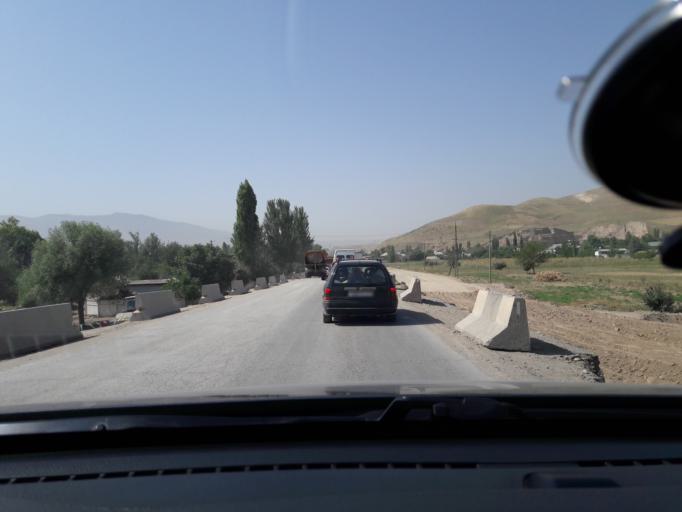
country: TJ
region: Dushanbe
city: Boshkengash
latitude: 38.4495
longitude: 68.7343
